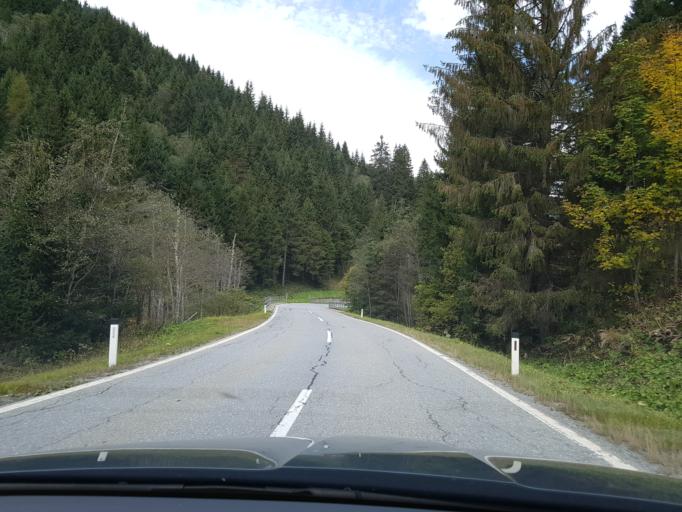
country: AT
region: Salzburg
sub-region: Politischer Bezirk Tamsweg
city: Ramingstein
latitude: 47.0215
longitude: 13.8992
